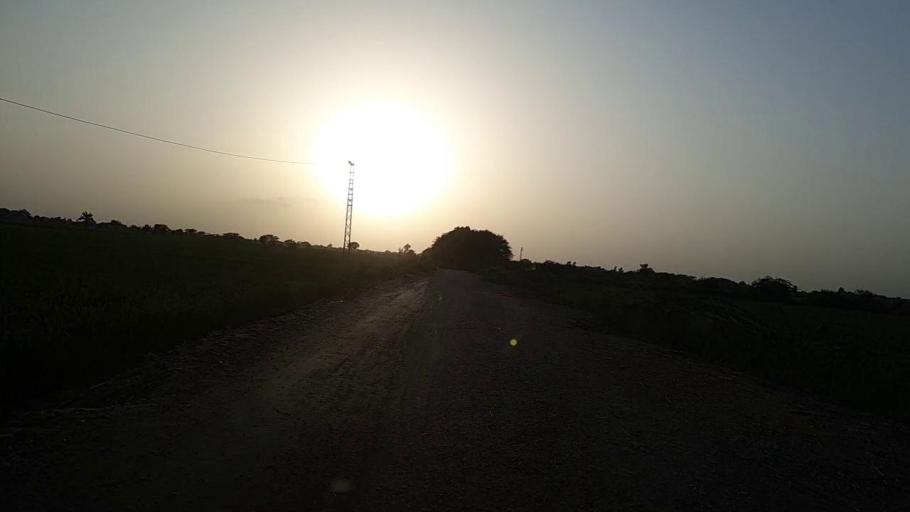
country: PK
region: Sindh
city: Kario
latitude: 24.7244
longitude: 68.4620
